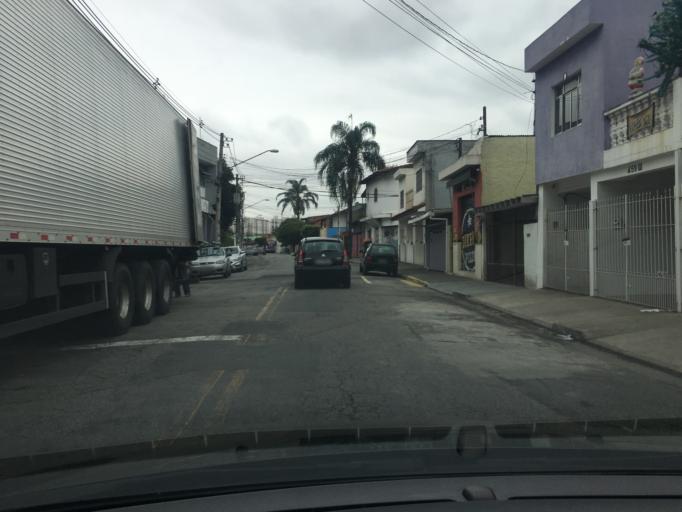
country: BR
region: Sao Paulo
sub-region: Guarulhos
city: Guarulhos
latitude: -23.4928
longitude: -46.5483
